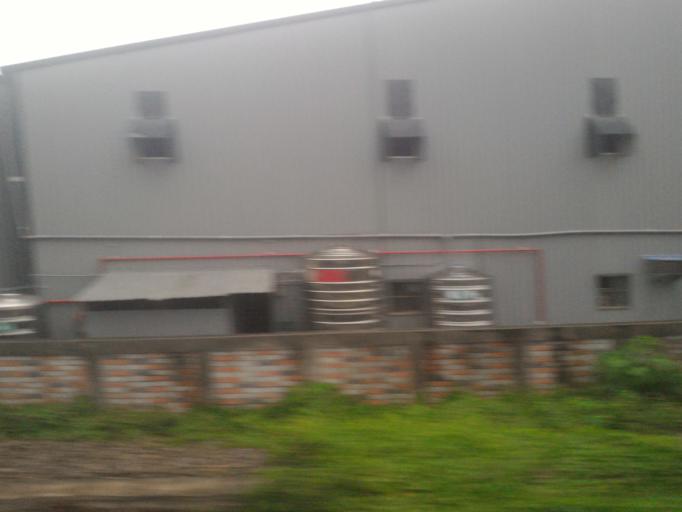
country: TW
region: Taipei
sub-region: Taipei
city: Banqiao
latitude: 25.0006
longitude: 121.4293
